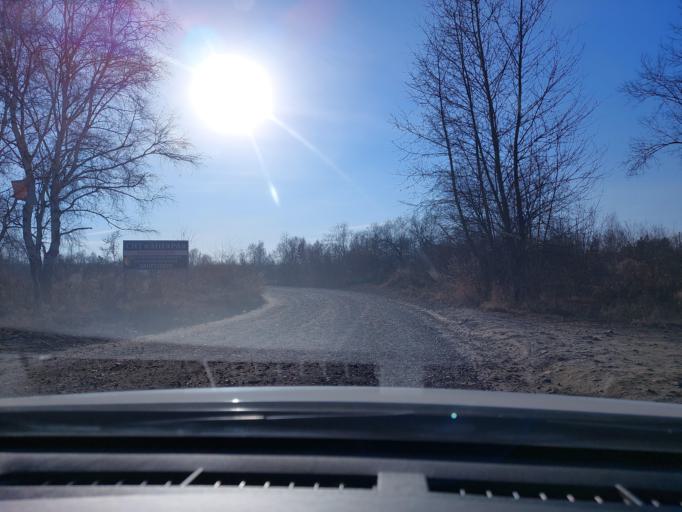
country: RU
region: Irkutsk
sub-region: Irkutskiy Rayon
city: Irkutsk
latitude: 52.3014
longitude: 104.2759
